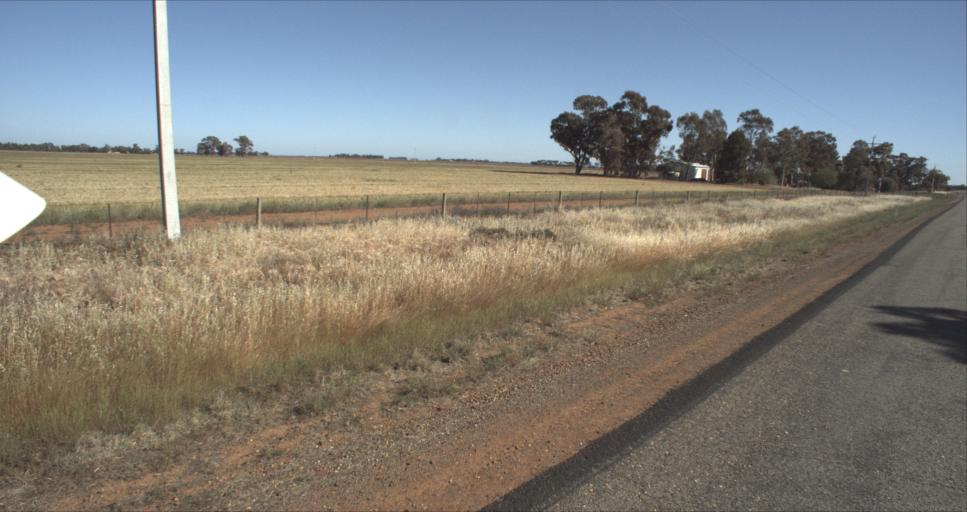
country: AU
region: New South Wales
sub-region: Leeton
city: Leeton
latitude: -34.5798
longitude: 146.2618
